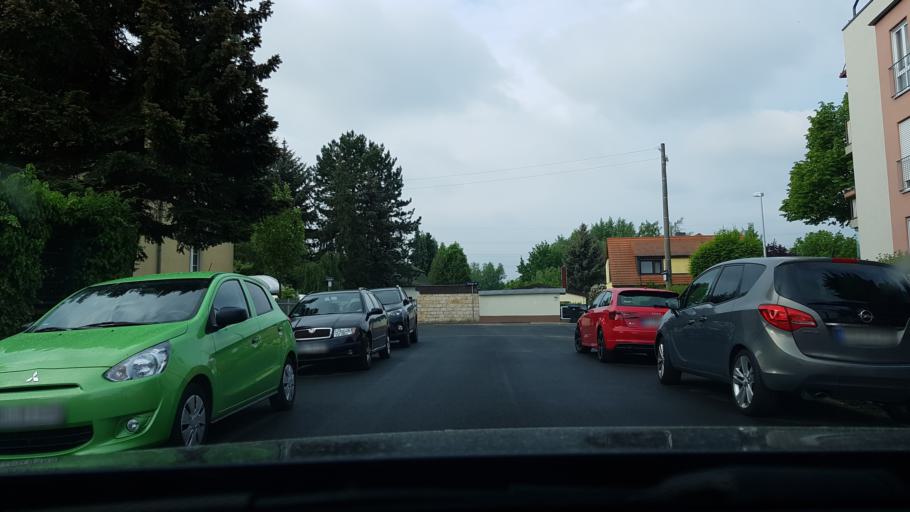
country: DE
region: Saxony
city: Heidenau
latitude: 51.0181
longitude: 13.8355
